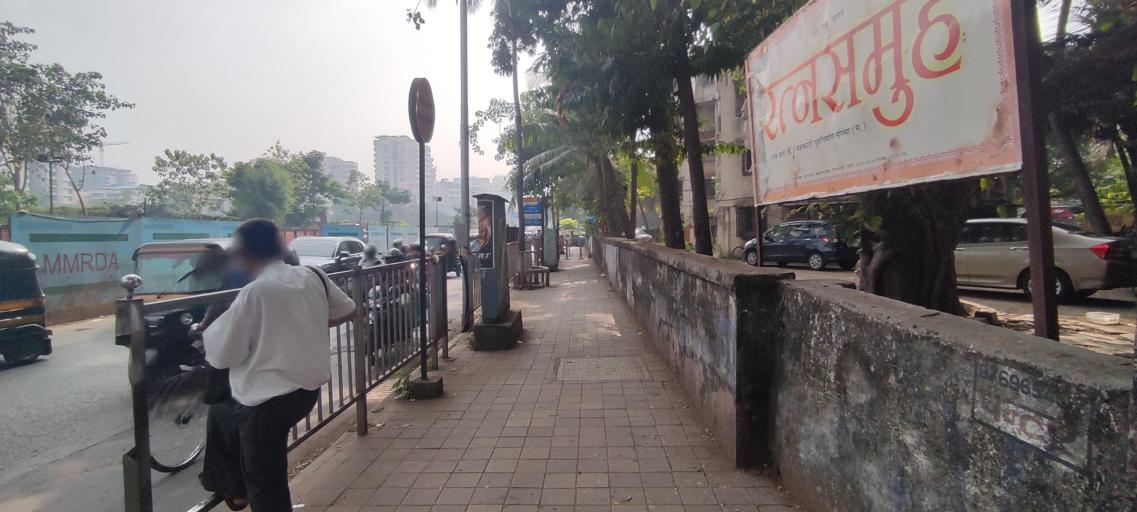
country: IN
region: Maharashtra
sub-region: Mumbai Suburban
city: Mumbai
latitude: 19.1182
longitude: 72.8297
